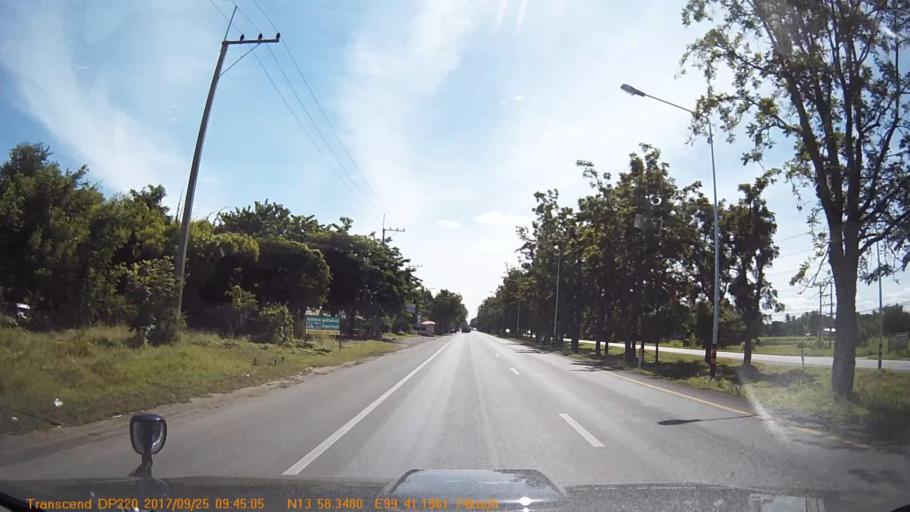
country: TH
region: Kanchanaburi
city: Tha Muang
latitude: 13.9724
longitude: 99.6869
